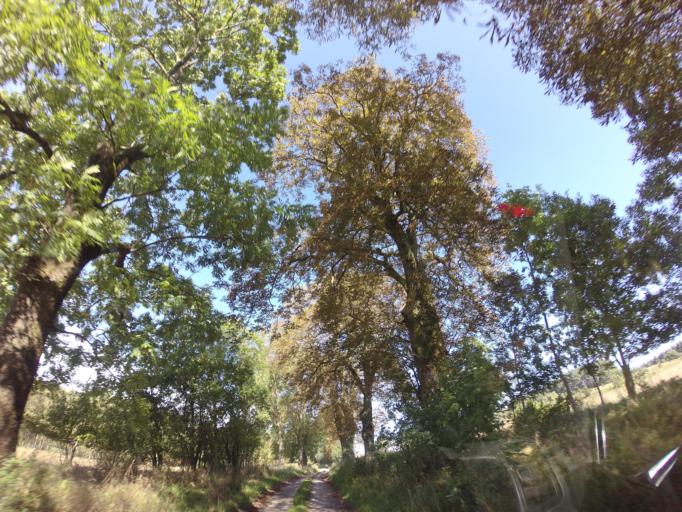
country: PL
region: West Pomeranian Voivodeship
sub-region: Powiat choszczenski
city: Recz
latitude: 53.1931
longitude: 15.5069
